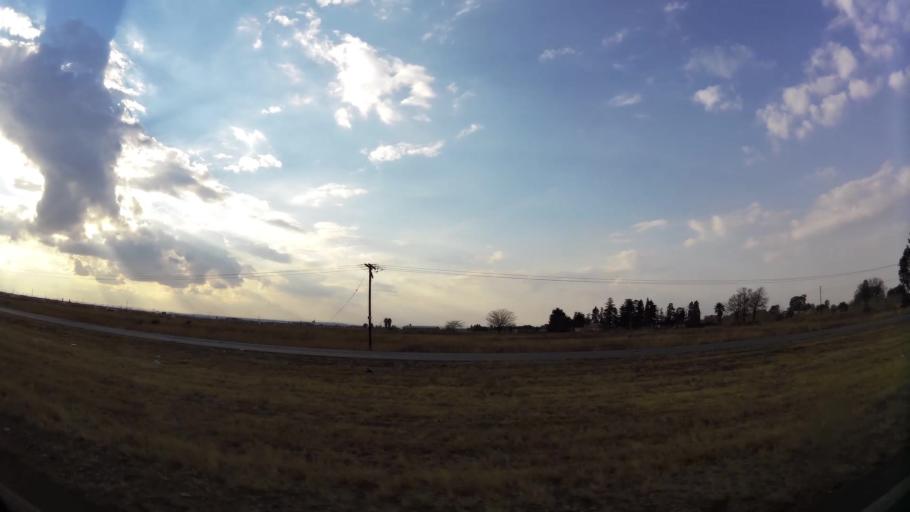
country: ZA
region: Gauteng
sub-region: Sedibeng District Municipality
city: Vanderbijlpark
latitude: -26.6196
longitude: 27.8159
